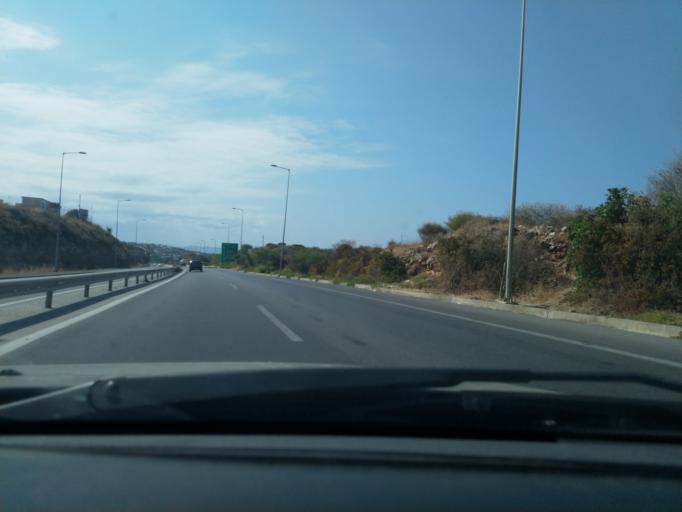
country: GR
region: Crete
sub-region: Nomos Rethymnis
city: Rethymno
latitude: 35.3578
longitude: 24.4627
